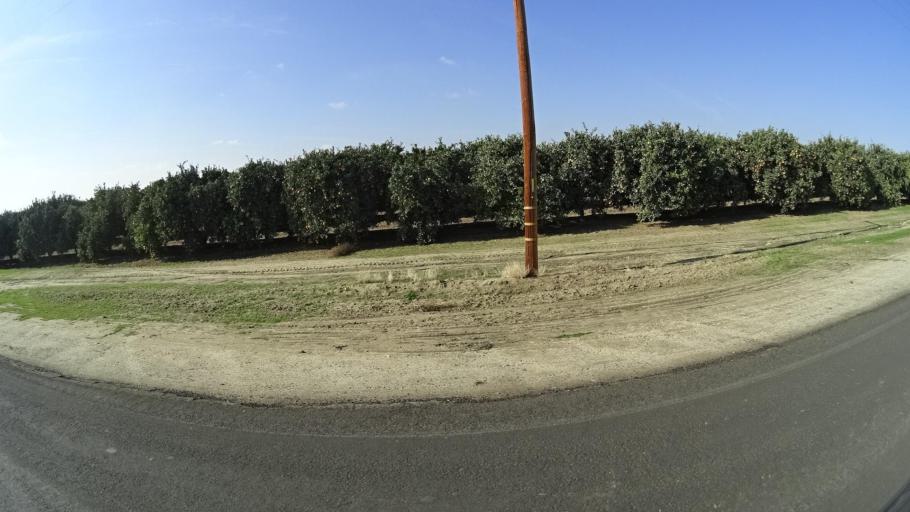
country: US
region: California
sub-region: Kern County
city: Arvin
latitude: 35.2692
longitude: -118.7707
